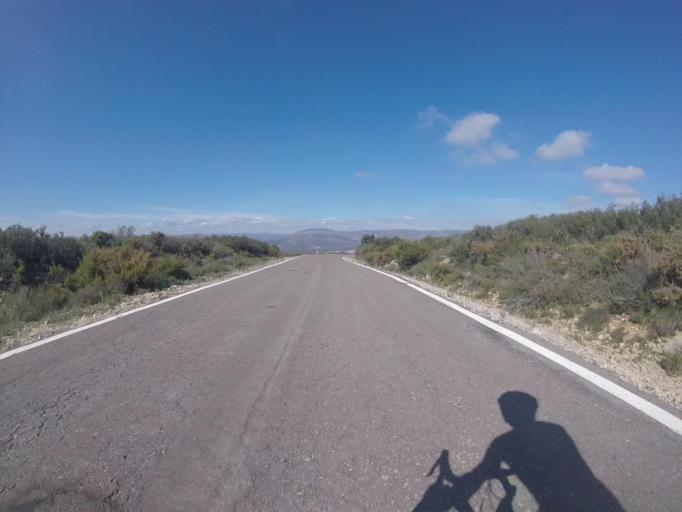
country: ES
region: Valencia
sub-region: Provincia de Castello
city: Albocasser
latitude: 40.3460
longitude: 0.0485
